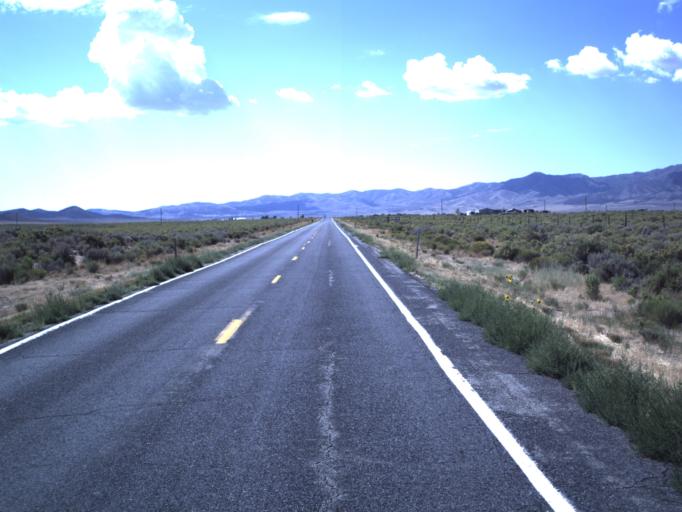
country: US
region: Utah
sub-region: Tooele County
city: Tooele
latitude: 40.1237
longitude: -112.4308
